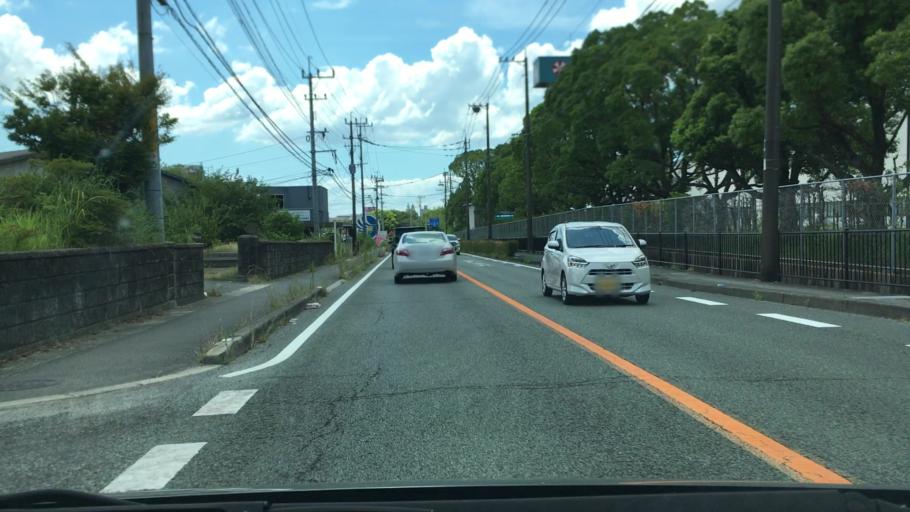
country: JP
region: Saga Prefecture
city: Kanzakimachi-kanzaki
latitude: 33.3391
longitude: 130.4312
